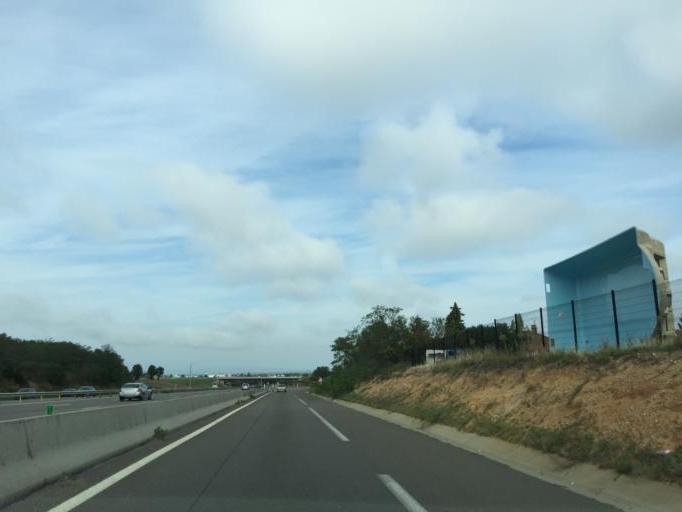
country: FR
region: Rhone-Alpes
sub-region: Departement de la Loire
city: La Fouillouse
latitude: 45.5193
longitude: 4.2959
